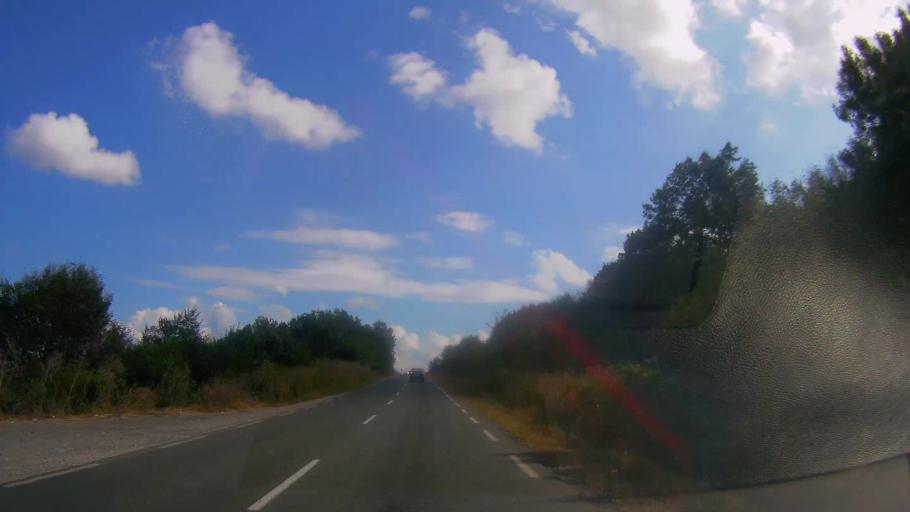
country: BG
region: Burgas
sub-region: Obshtina Kameno
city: Kameno
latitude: 42.4842
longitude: 27.3431
